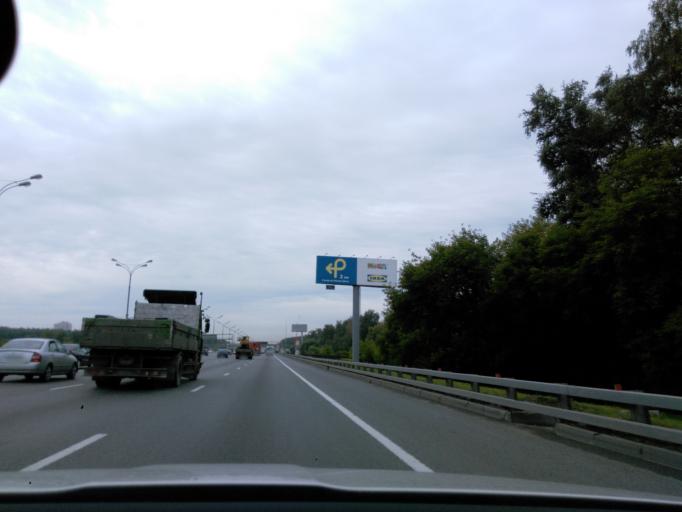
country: RU
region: Moscow
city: Zhulebino
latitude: 55.6737
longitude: 37.8359
